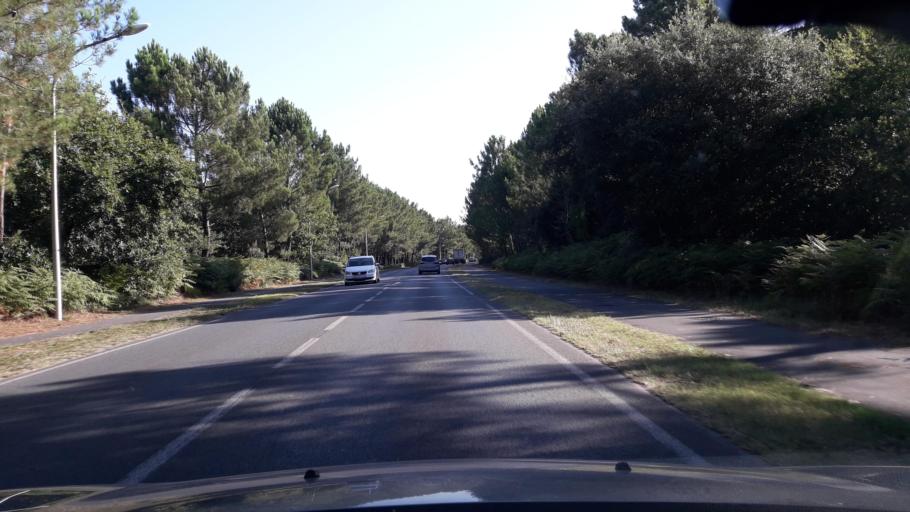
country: FR
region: Poitou-Charentes
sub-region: Departement de la Charente-Maritime
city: Les Mathes
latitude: 45.7061
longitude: -1.1640
